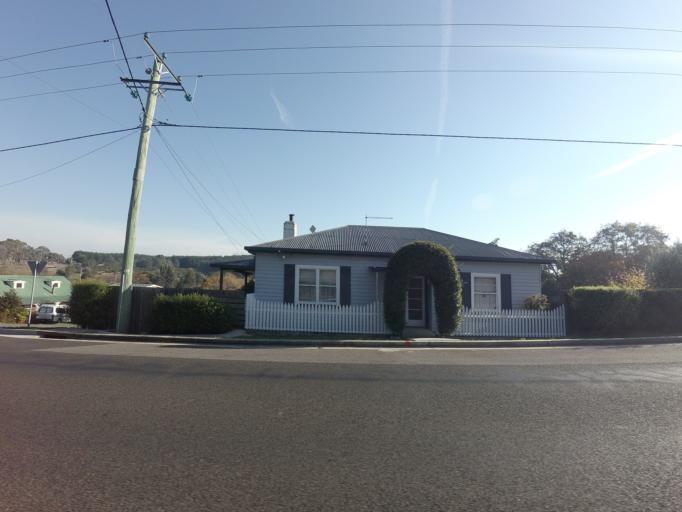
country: AU
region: Tasmania
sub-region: Northern Midlands
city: Longford
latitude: -41.5328
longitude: 147.0065
